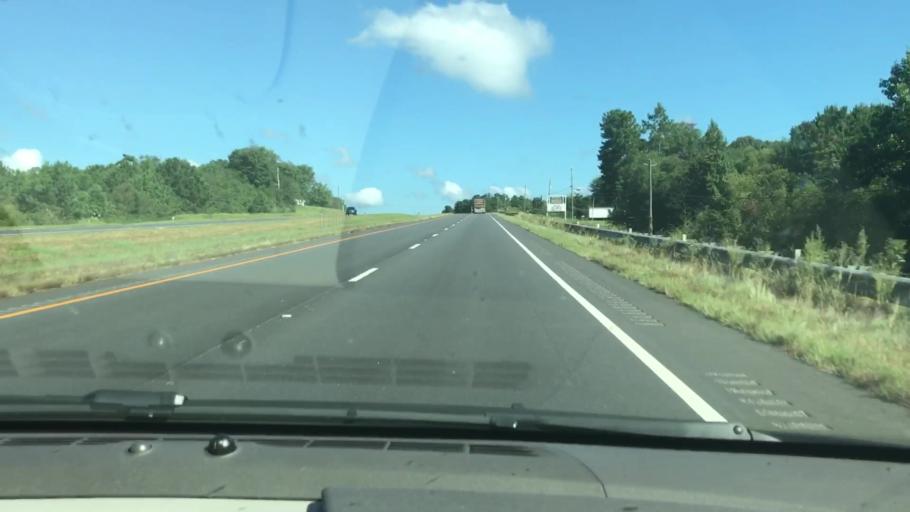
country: US
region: Alabama
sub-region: Barbour County
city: Eufaula
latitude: 32.0255
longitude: -85.1196
